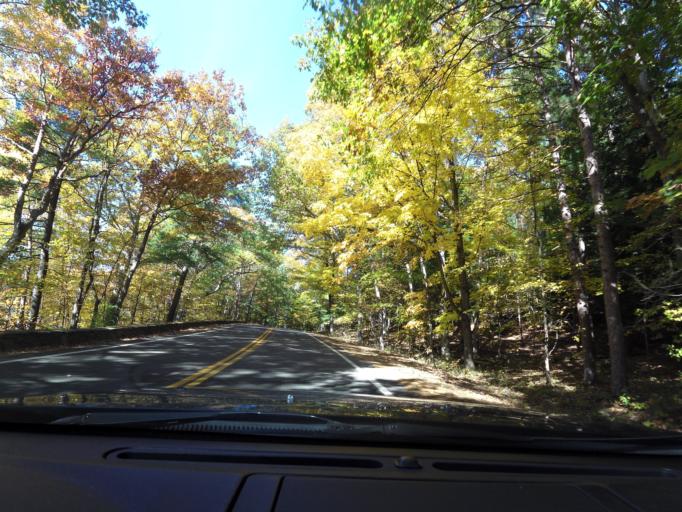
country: US
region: New York
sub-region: Wyoming County
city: Castile
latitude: 42.6135
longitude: -78.0091
